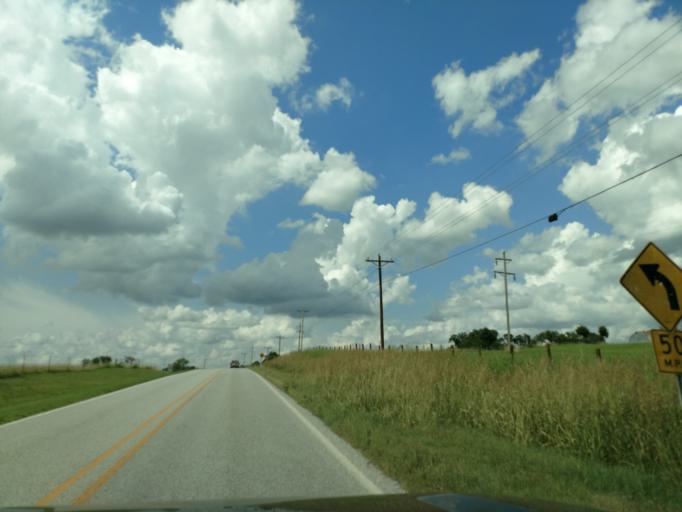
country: US
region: Arkansas
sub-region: Carroll County
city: Berryville
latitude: 36.4668
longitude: -93.5557
